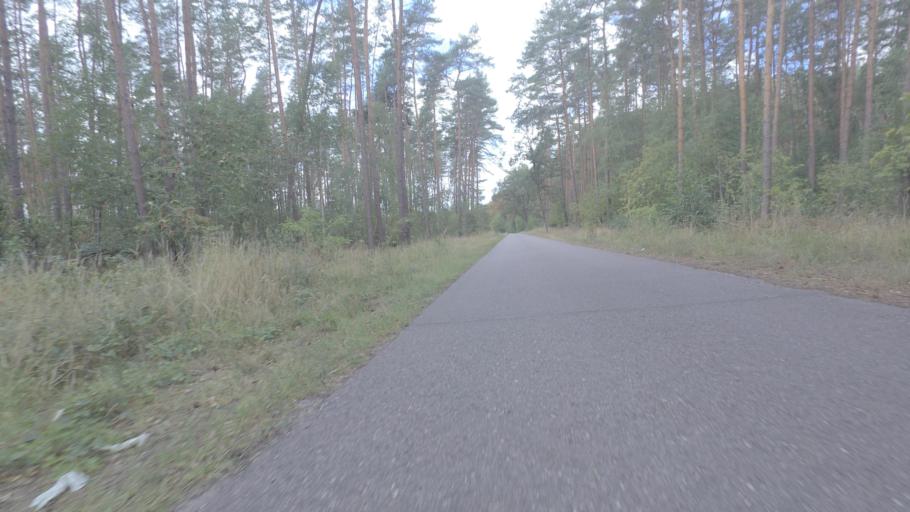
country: DE
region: Brandenburg
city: Wittstock
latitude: 53.0781
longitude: 12.4911
